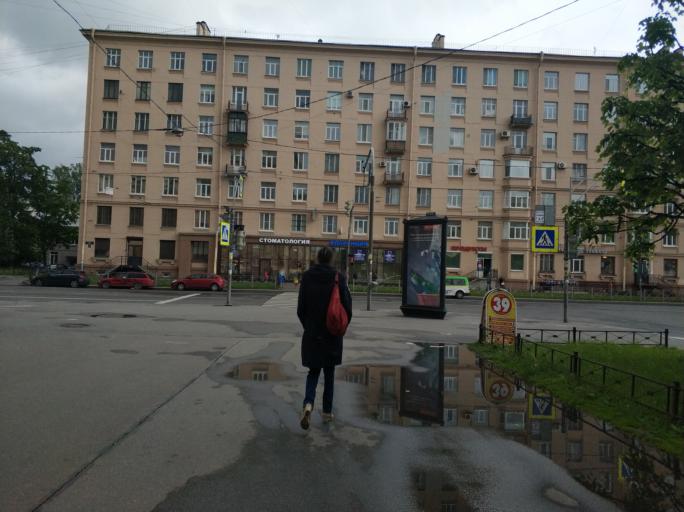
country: RU
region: St.-Petersburg
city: Kupchino
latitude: 59.8536
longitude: 30.3291
